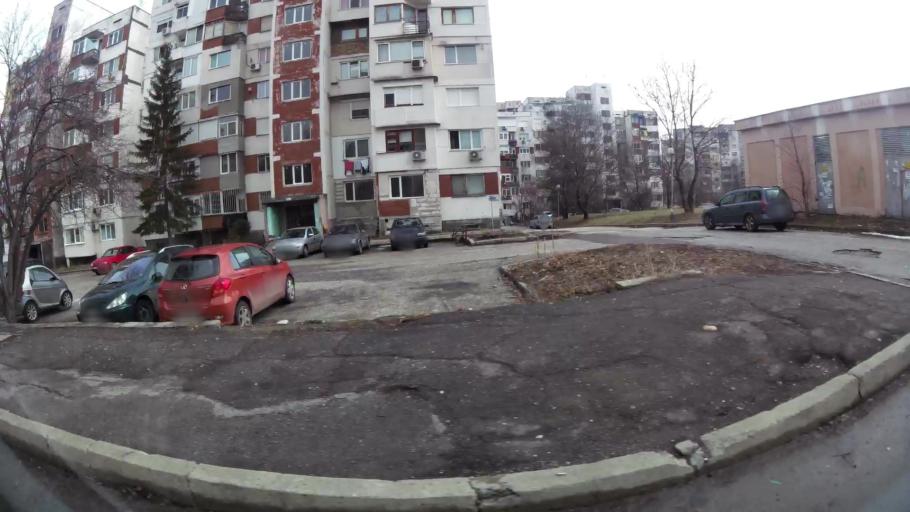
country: BG
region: Sofiya
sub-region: Obshtina Bozhurishte
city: Bozhurishte
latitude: 42.7159
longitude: 23.2410
